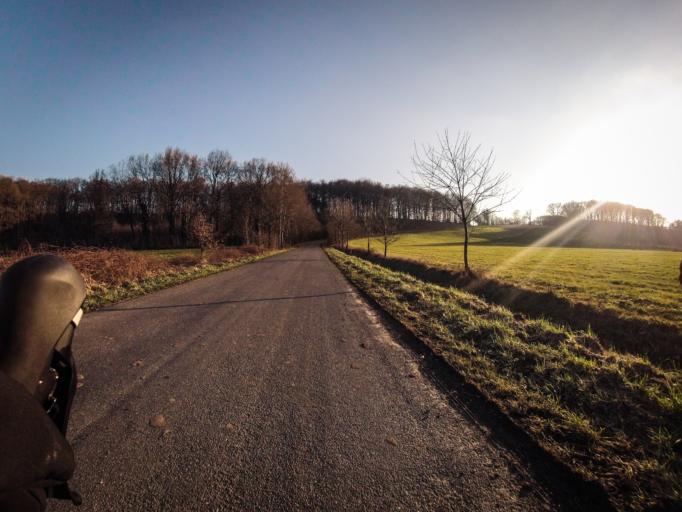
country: DE
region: North Rhine-Westphalia
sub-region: Regierungsbezirk Munster
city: Tecklenburg
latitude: 52.2490
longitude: 7.8326
